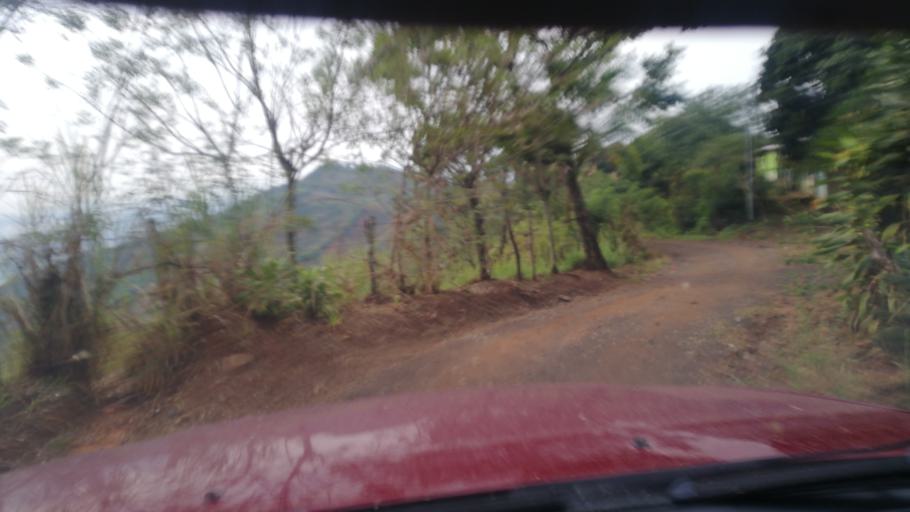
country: CO
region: Risaralda
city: Balboa
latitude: 4.8846
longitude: -75.9497
